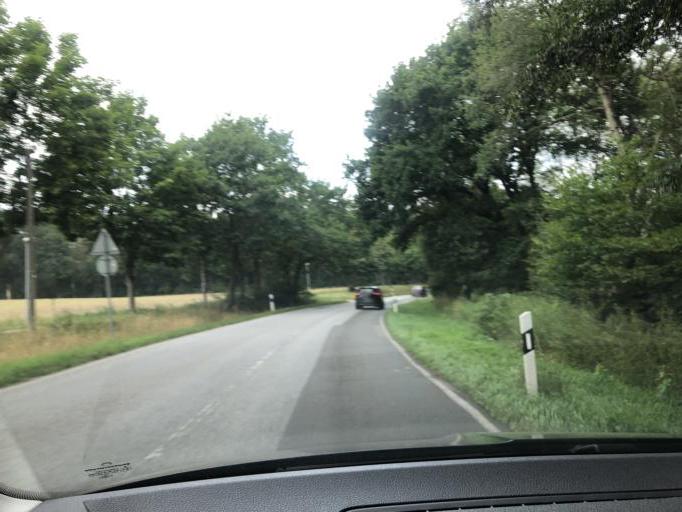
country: DE
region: Mecklenburg-Vorpommern
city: Stralendorf
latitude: 53.5709
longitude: 11.3314
